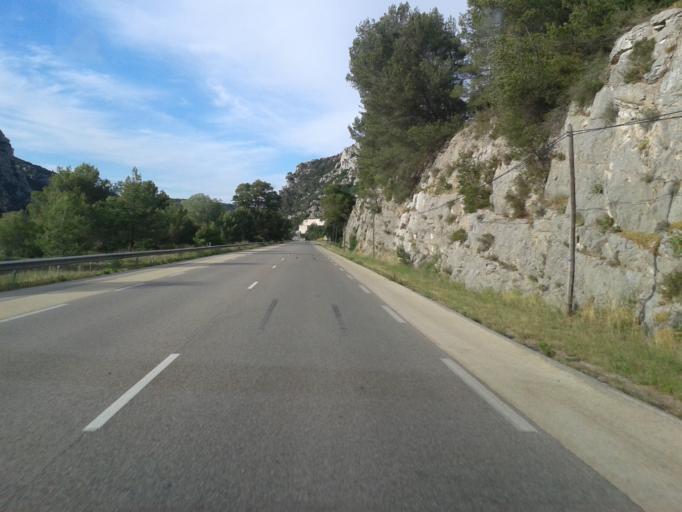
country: FR
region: Provence-Alpes-Cote d'Azur
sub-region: Departement des Bouches-du-Rhone
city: Jouques
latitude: 43.6754
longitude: 5.6516
